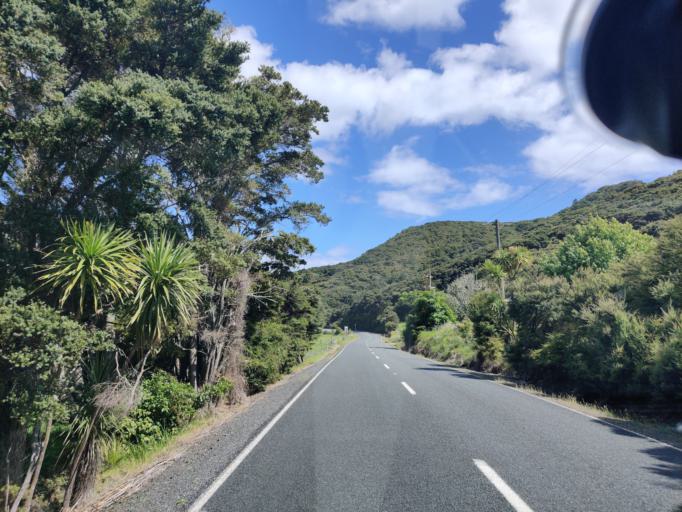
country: NZ
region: Northland
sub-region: Far North District
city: Paihia
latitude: -35.2646
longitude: 174.2690
